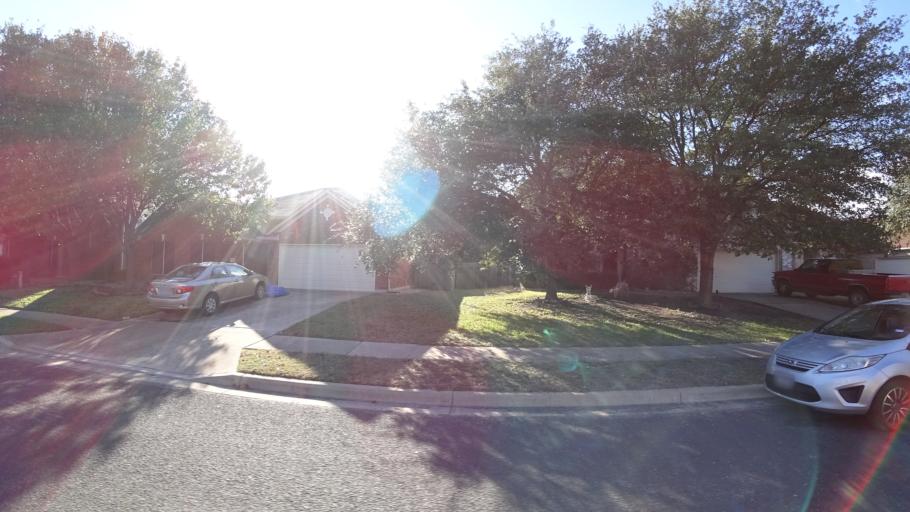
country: US
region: Texas
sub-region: Williamson County
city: Brushy Creek
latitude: 30.4940
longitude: -97.7464
